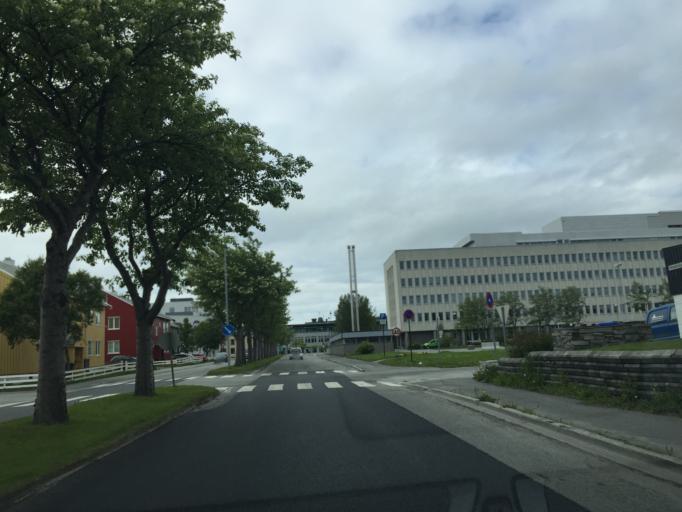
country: NO
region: Nordland
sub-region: Bodo
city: Bodo
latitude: 67.2793
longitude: 14.3769
